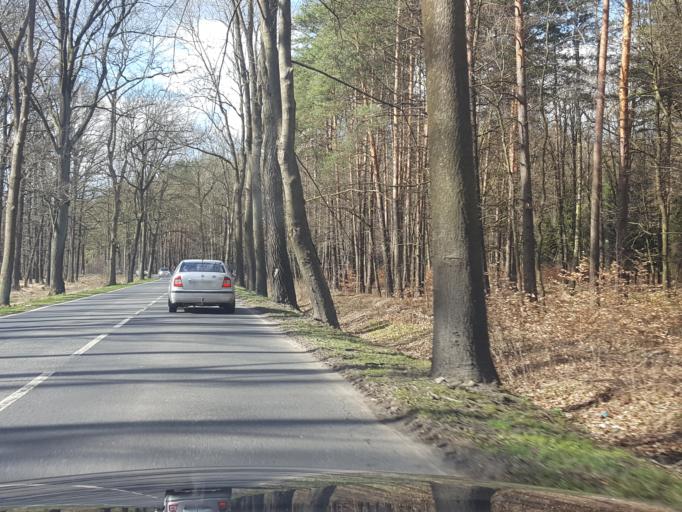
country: PL
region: Silesian Voivodeship
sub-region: Powiat pszczynski
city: Kobior
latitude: 50.0702
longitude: 18.9124
